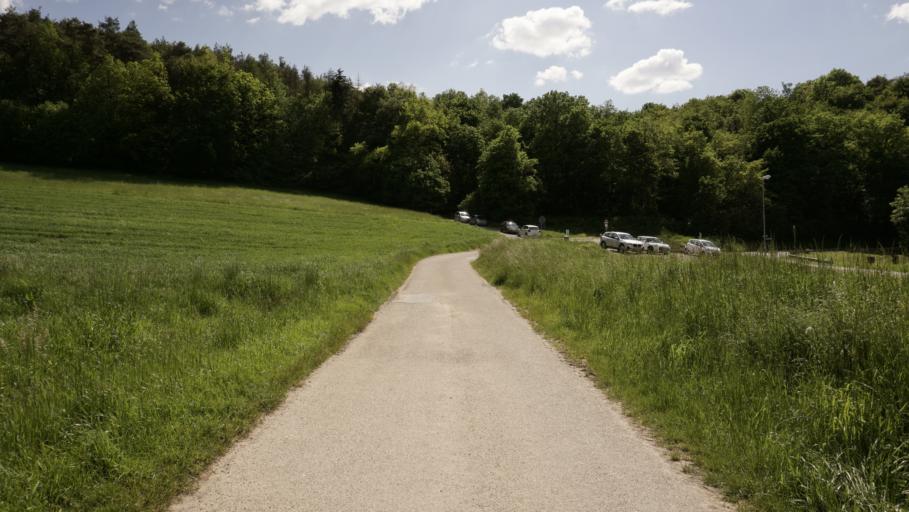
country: DE
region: Baden-Wuerttemberg
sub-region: Karlsruhe Region
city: Billigheim
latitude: 49.3841
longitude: 9.2050
